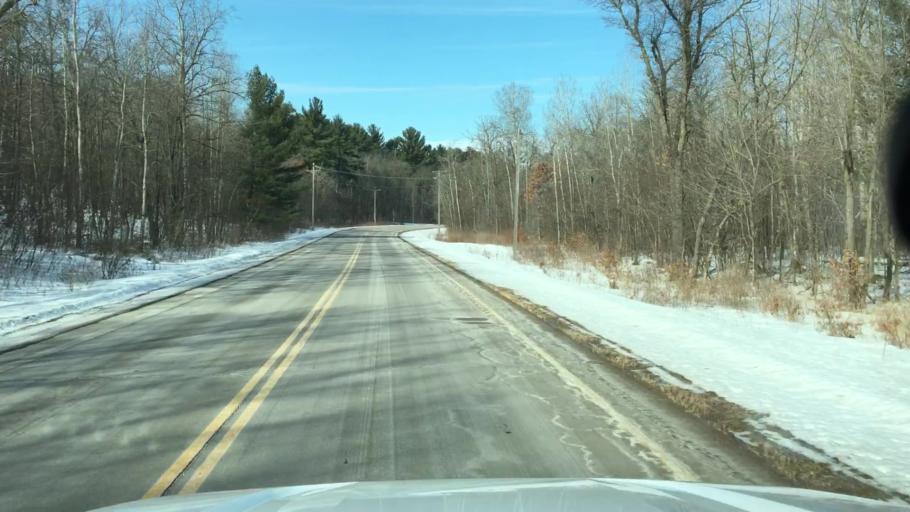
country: US
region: Wisconsin
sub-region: Polk County
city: Saint Croix Falls
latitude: 45.4647
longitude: -92.6845
